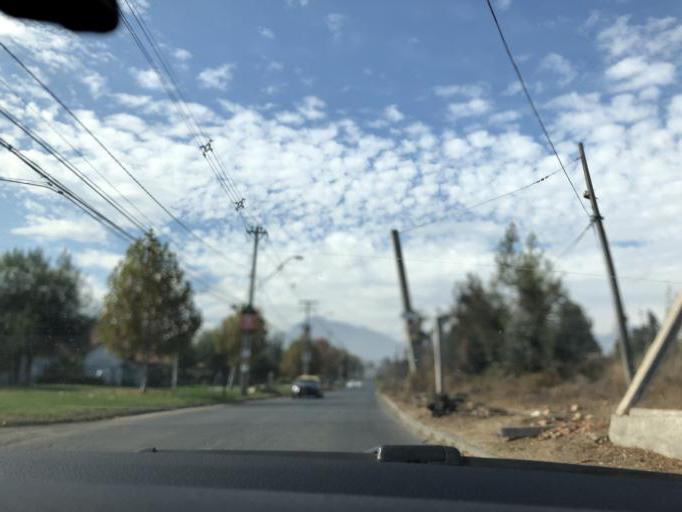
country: CL
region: Santiago Metropolitan
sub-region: Provincia de Cordillera
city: Puente Alto
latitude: -33.5717
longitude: -70.5500
